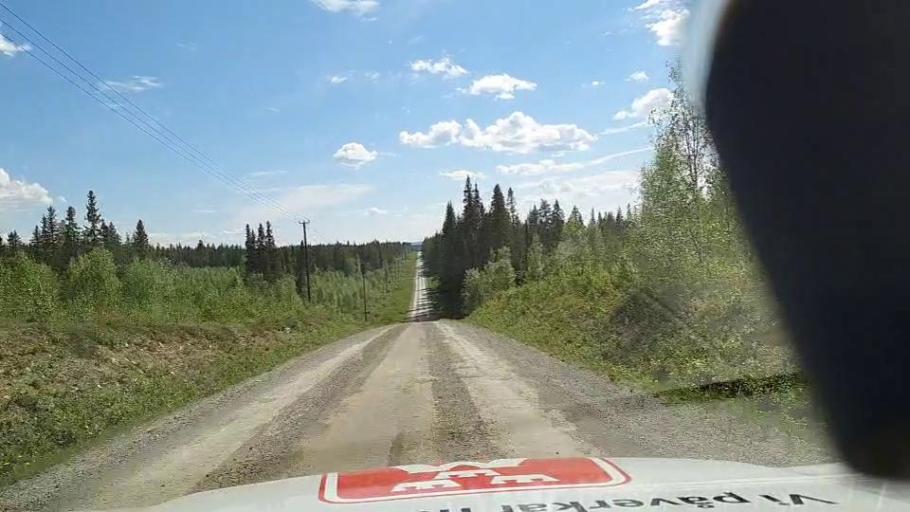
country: SE
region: Jaemtland
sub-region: Stroemsunds Kommun
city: Stroemsund
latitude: 64.4861
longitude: 15.5915
